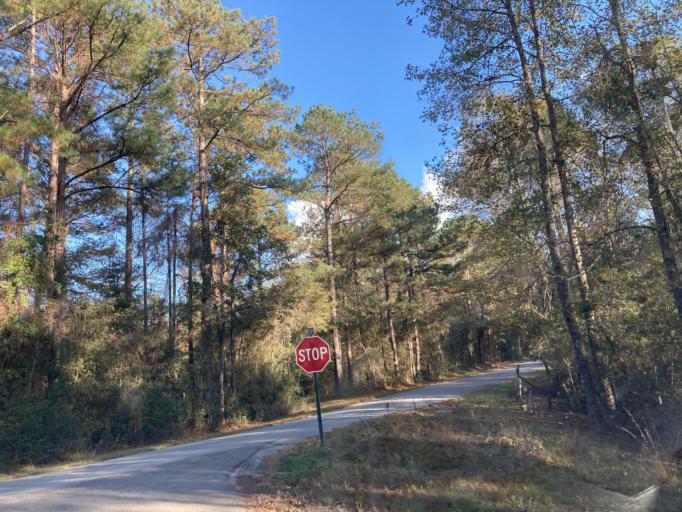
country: US
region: Mississippi
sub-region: Lamar County
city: Sumrall
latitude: 31.3989
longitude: -89.6502
